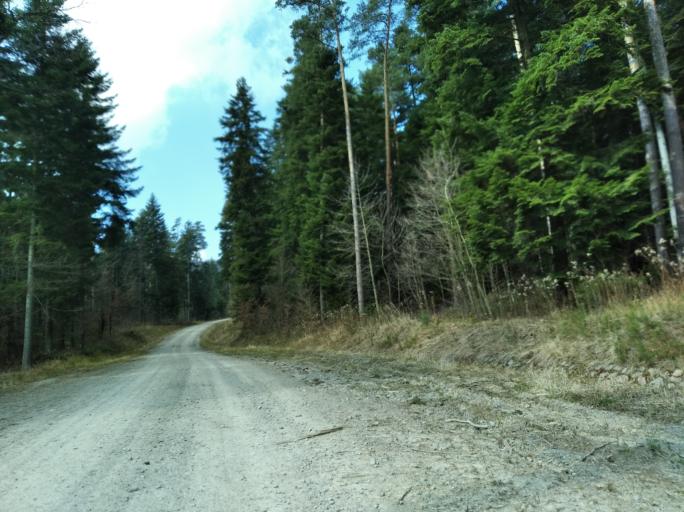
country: PL
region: Subcarpathian Voivodeship
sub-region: Powiat strzyzowski
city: Strzyzow
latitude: 49.8127
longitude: 21.8240
